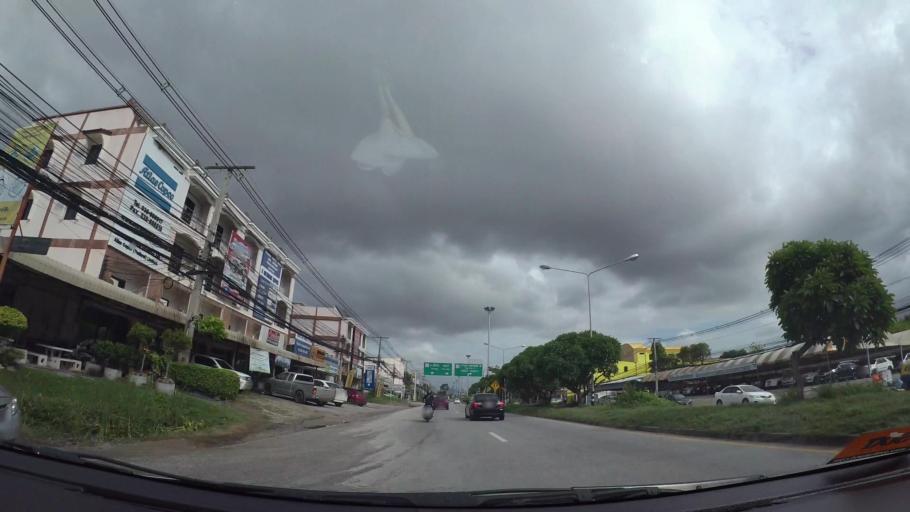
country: TH
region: Rayong
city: Rayong
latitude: 12.6888
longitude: 101.2095
